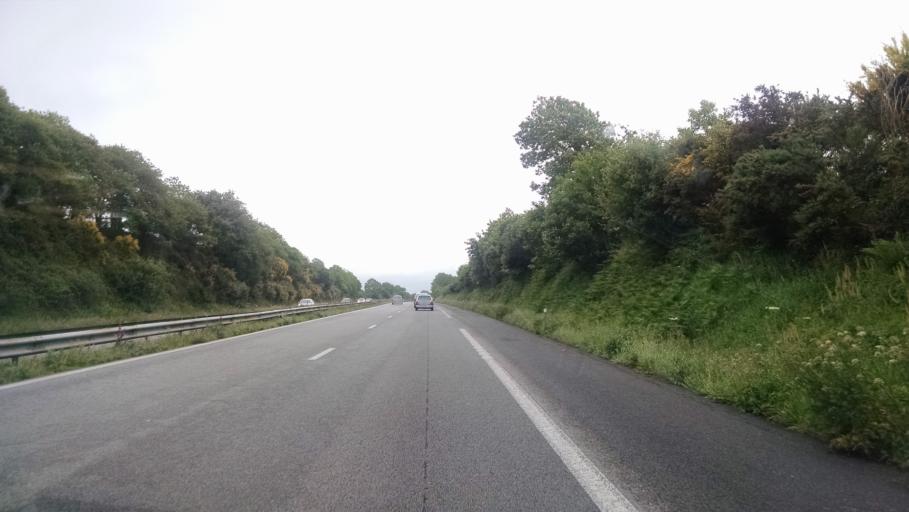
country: FR
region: Brittany
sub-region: Departement du Finistere
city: Saint-Yvi
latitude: 47.9330
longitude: -3.9068
